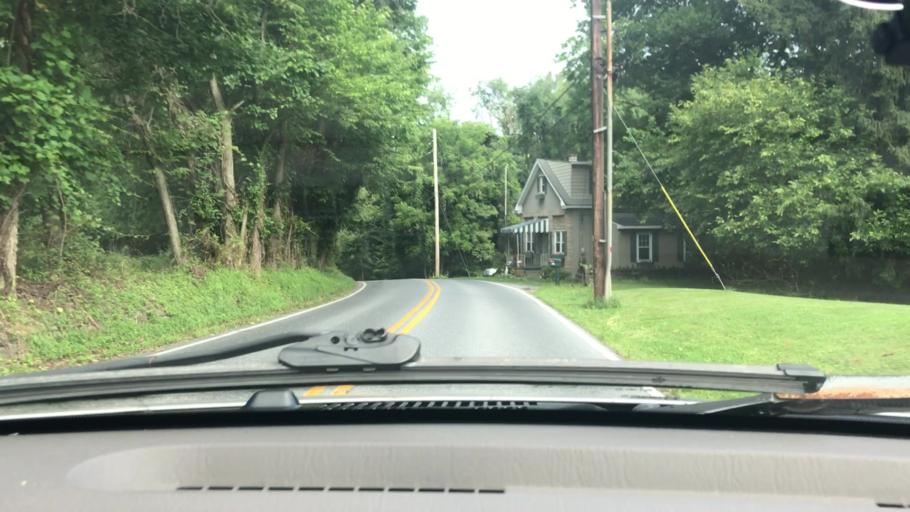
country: US
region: Pennsylvania
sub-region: Dauphin County
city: Highspire
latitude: 40.2074
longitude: -76.7617
